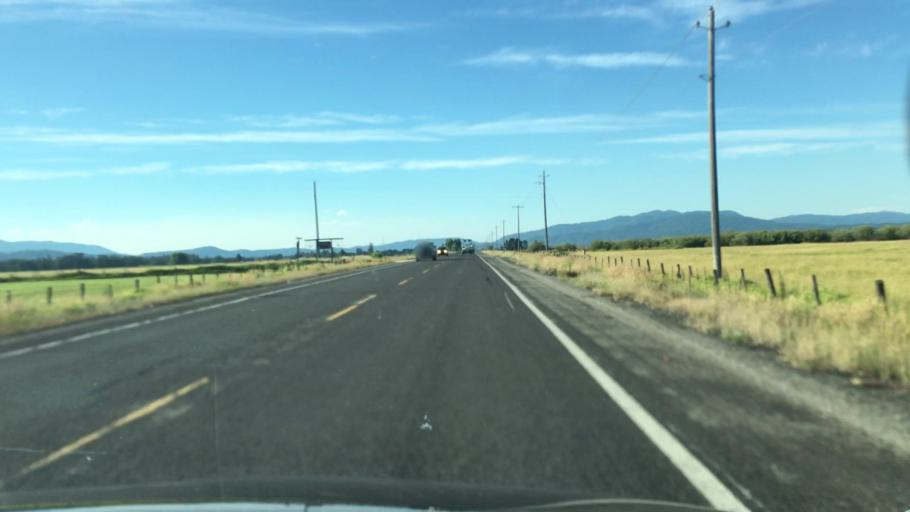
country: US
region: Idaho
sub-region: Valley County
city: Cascade
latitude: 44.4168
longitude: -115.9999
